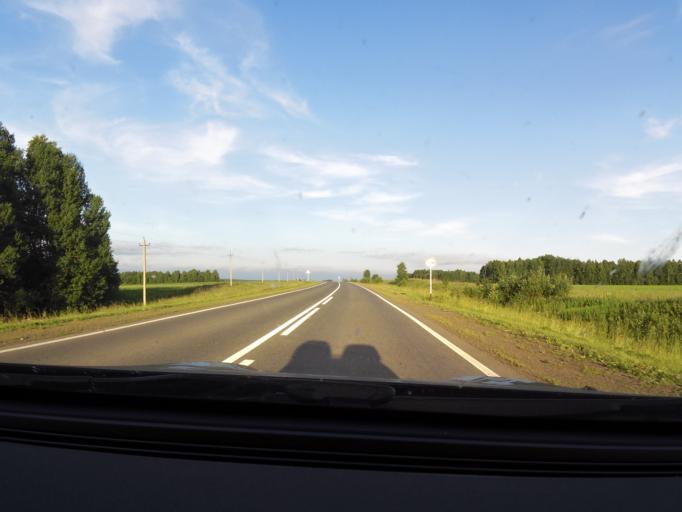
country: RU
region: Perm
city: Siva
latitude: 58.5273
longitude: 53.9865
